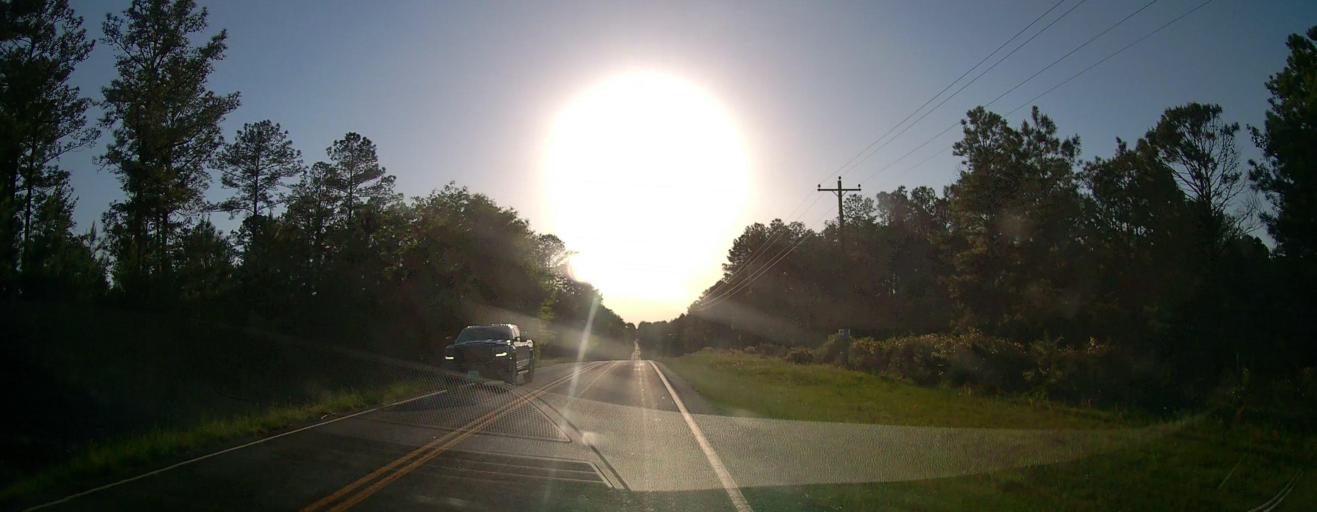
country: US
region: Georgia
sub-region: Schley County
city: Ellaville
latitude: 32.3217
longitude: -84.2245
